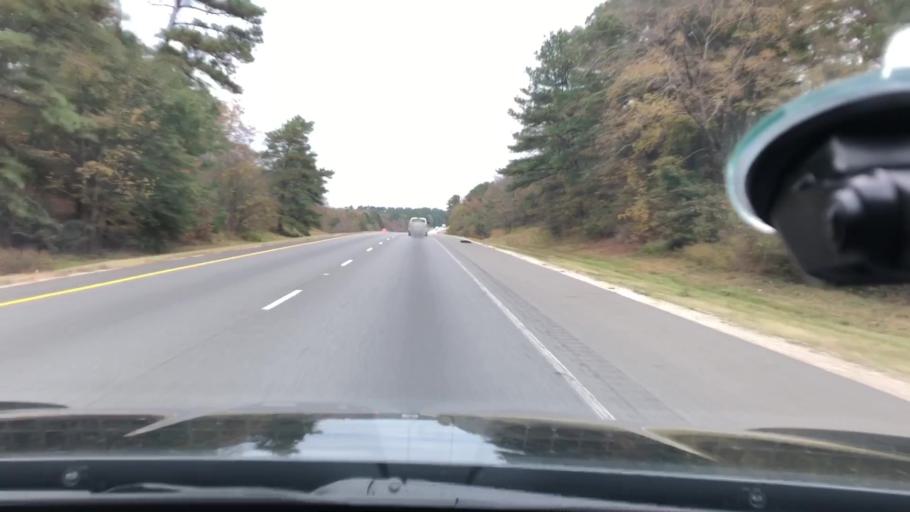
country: US
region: Arkansas
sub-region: Hot Spring County
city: Malvern
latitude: 34.3108
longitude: -92.9385
